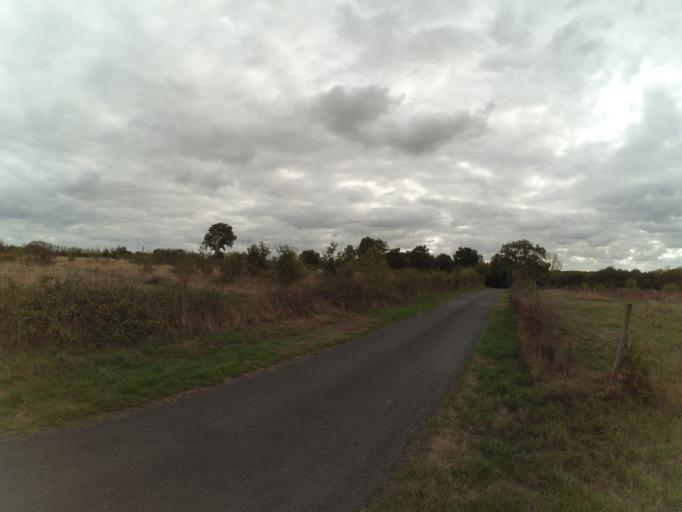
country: FR
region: Pays de la Loire
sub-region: Departement de la Loire-Atlantique
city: Remouille
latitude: 47.0531
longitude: -1.3475
